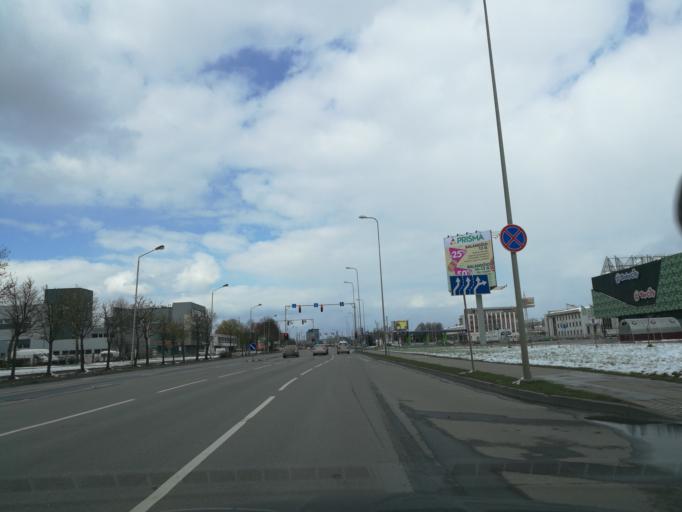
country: LT
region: Kauno apskritis
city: Dainava (Kaunas)
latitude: 54.9081
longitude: 23.9818
